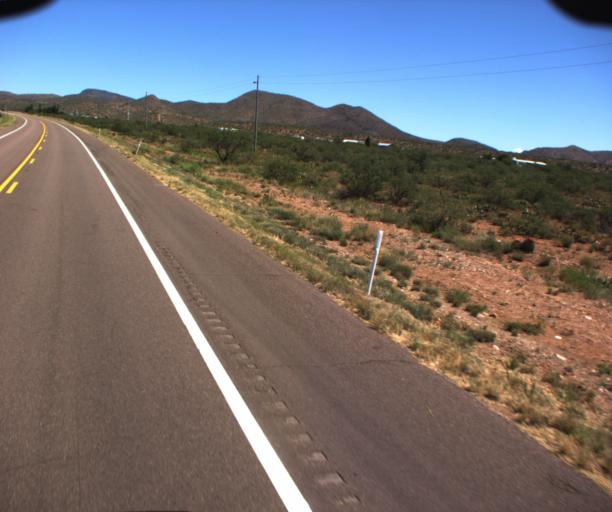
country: US
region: Arizona
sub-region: Gila County
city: Globe
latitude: 33.4306
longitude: -110.7255
